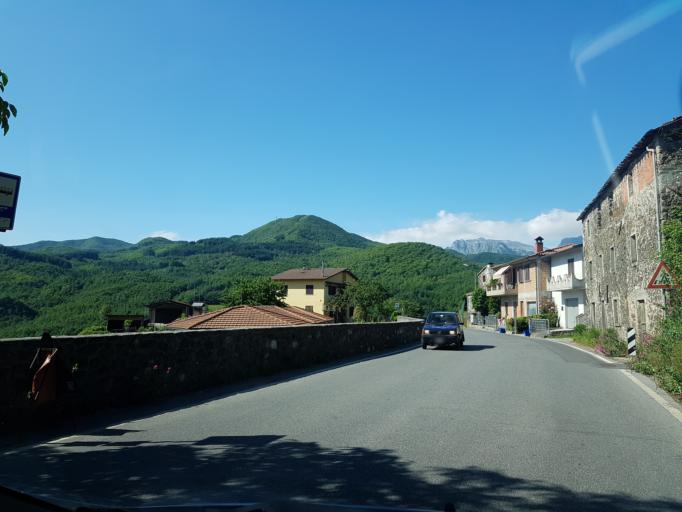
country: IT
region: Tuscany
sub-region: Provincia di Lucca
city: Piazza al Serchio-San Michele
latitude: 44.1864
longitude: 10.2912
